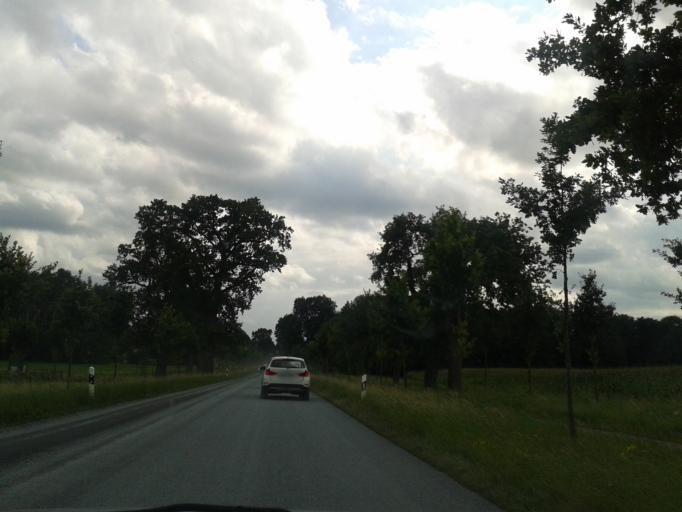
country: DE
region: North Rhine-Westphalia
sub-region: Regierungsbezirk Detmold
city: Schlangen
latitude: 51.8249
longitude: 8.8432
